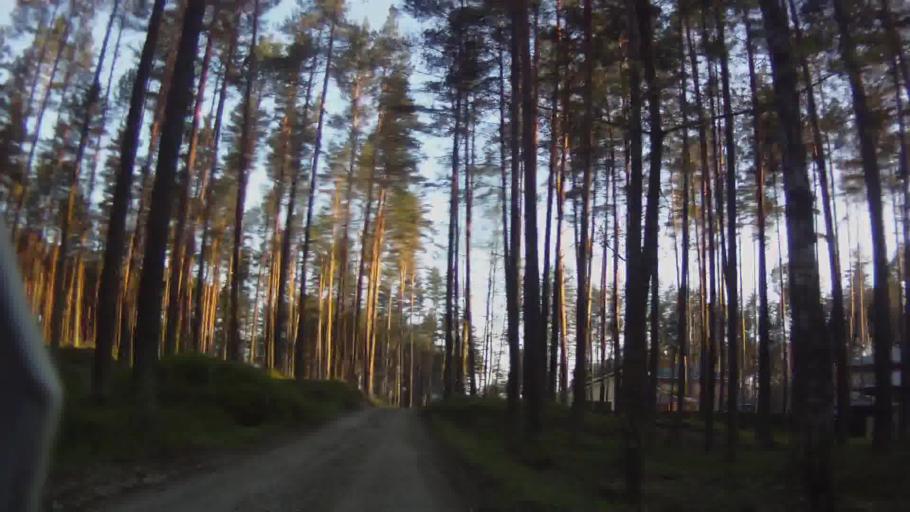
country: LV
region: Riga
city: Jaunciems
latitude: 57.0559
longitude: 24.1663
